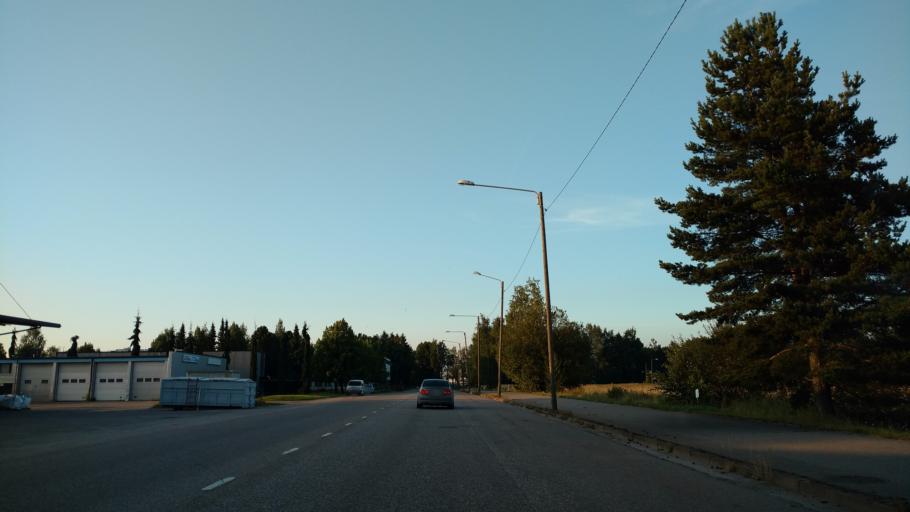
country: FI
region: Varsinais-Suomi
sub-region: Salo
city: Salo
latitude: 60.3771
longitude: 23.1176
